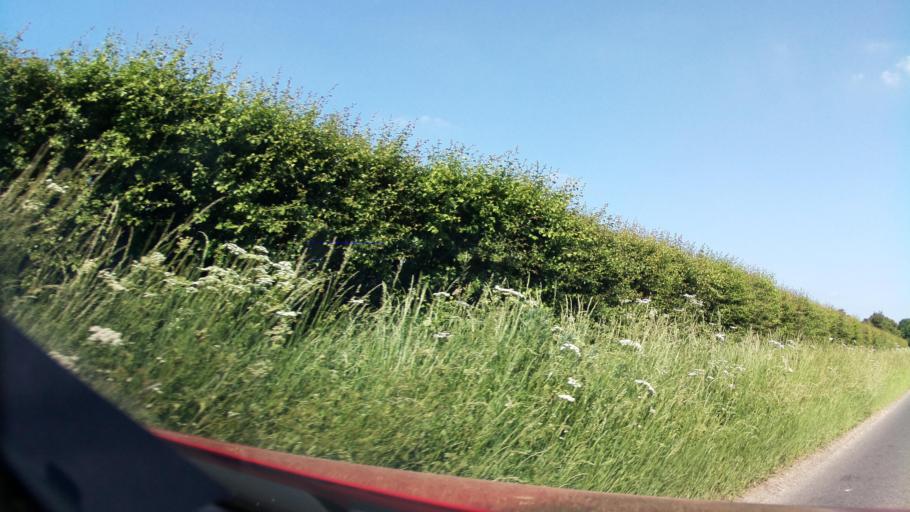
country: GB
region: England
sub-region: Hampshire
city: Andover
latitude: 51.2214
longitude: -1.5186
